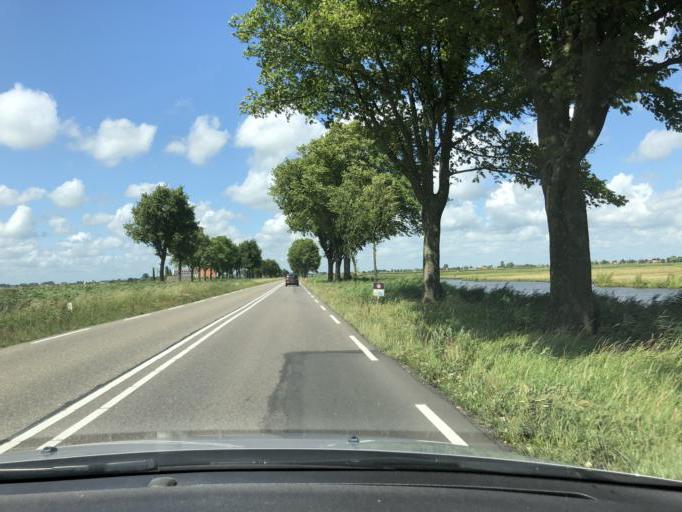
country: NL
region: North Holland
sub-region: Gemeente Edam-Volendam
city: Edam
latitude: 52.5542
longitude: 5.0151
